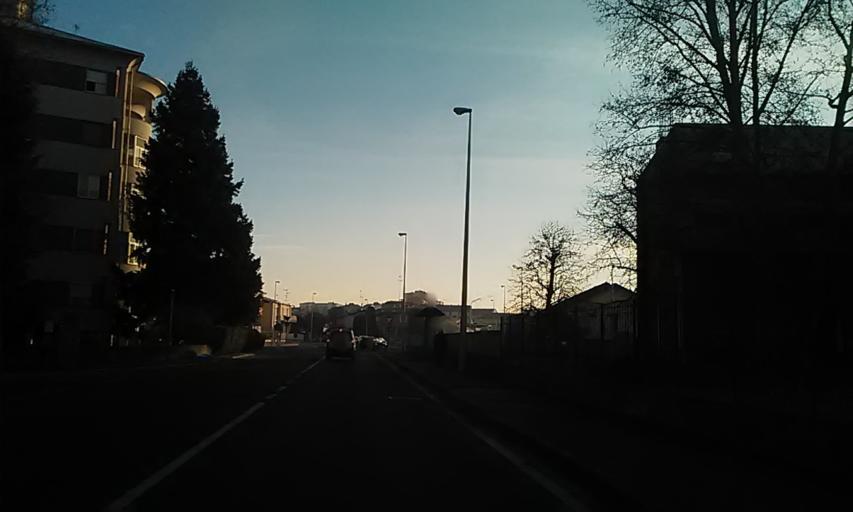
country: IT
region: Piedmont
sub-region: Provincia di Vercelli
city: Vercelli
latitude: 45.3177
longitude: 8.4065
